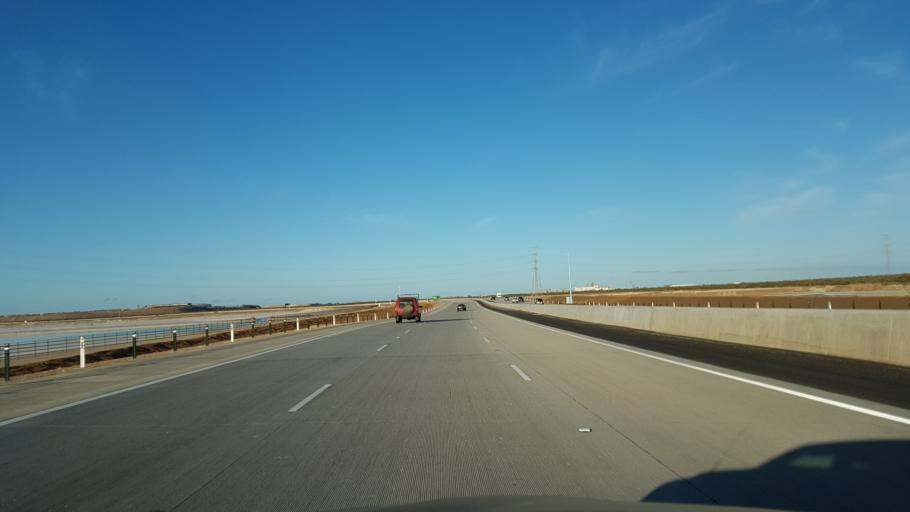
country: AU
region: South Australia
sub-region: Port Adelaide Enfield
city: Enfield
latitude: -34.8077
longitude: 138.5704
